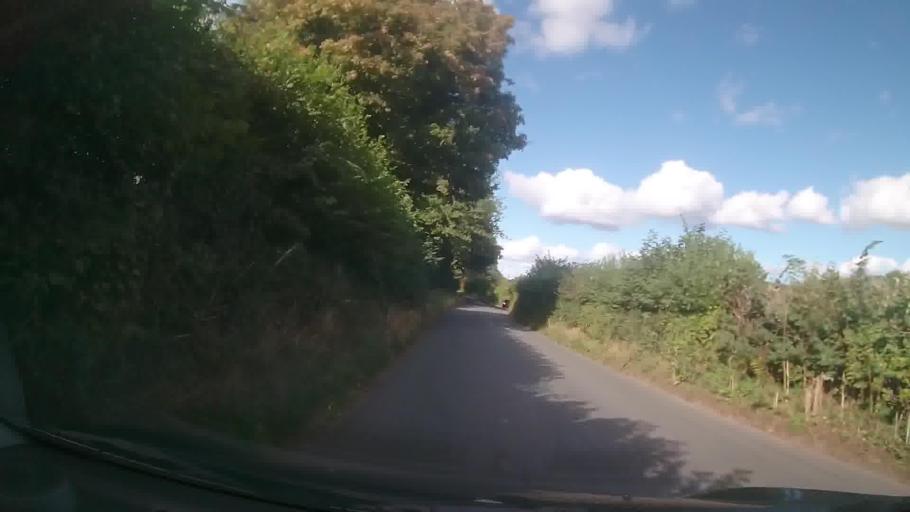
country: GB
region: Wales
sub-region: Sir Powys
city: Brecon
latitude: 51.8916
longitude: -3.2993
